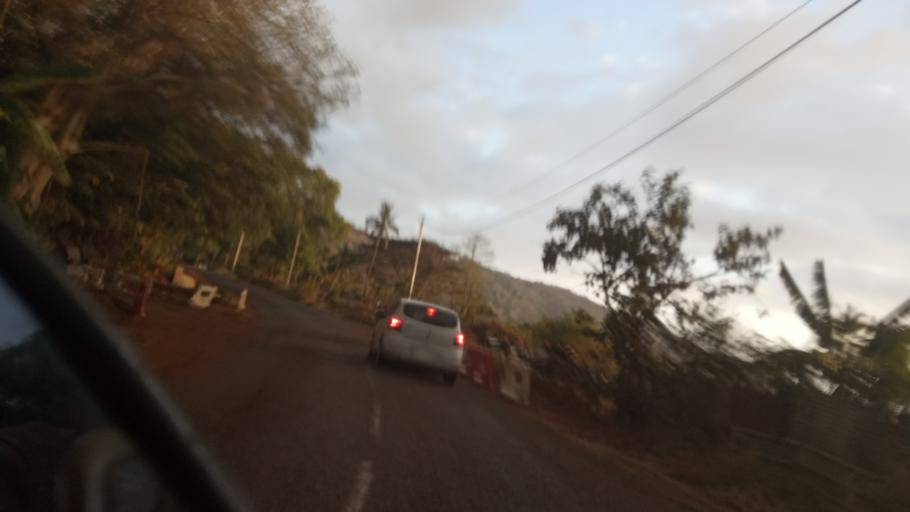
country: YT
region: Kani-Keli
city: Kani Keli
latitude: -12.9375
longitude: 45.1020
